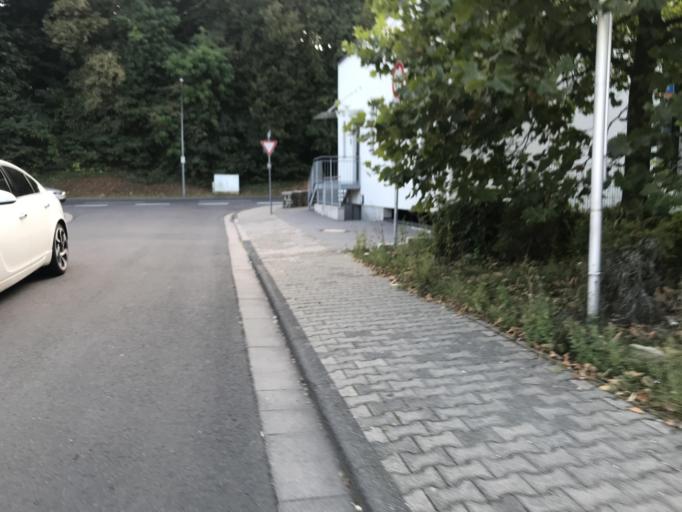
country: DE
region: Rheinland-Pfalz
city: Kirn
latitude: 49.7916
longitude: 7.4556
